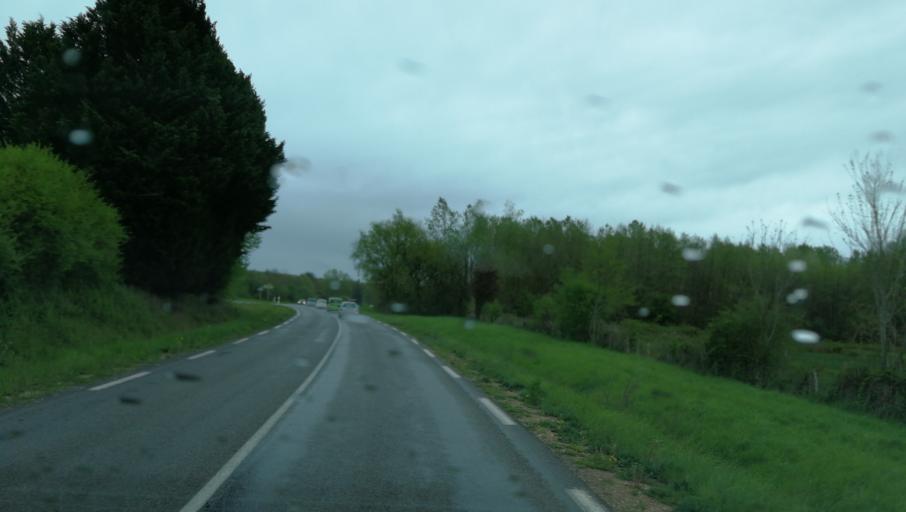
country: FR
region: Franche-Comte
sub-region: Departement du Jura
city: Bletterans
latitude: 46.7148
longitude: 5.4756
